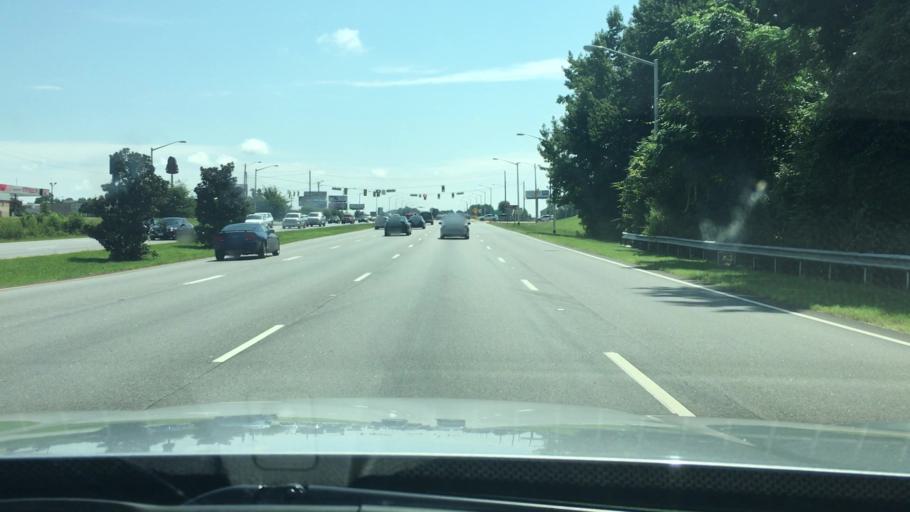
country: US
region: South Carolina
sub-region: Florence County
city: Florence
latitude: 34.1883
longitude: -79.8268
